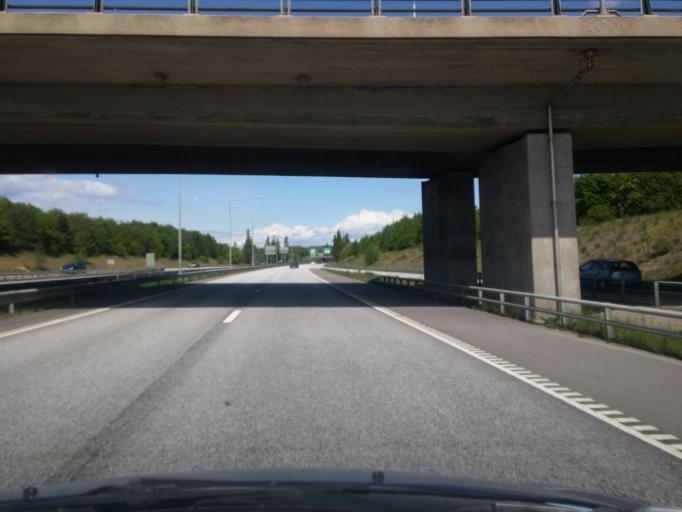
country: SE
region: Skane
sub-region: Malmo
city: Tygelsjo
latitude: 55.5549
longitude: 12.9996
